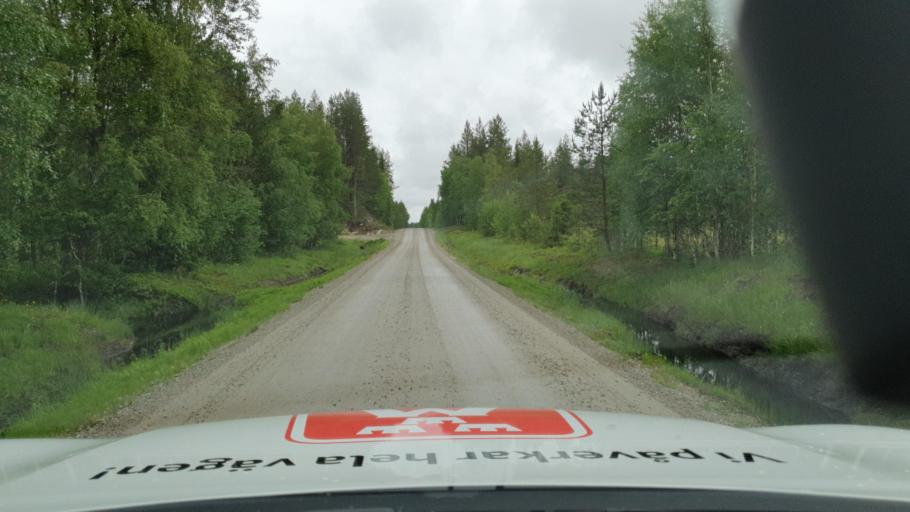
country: SE
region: Vaesterbotten
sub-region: Dorotea Kommun
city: Dorotea
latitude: 64.0005
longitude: 16.7990
